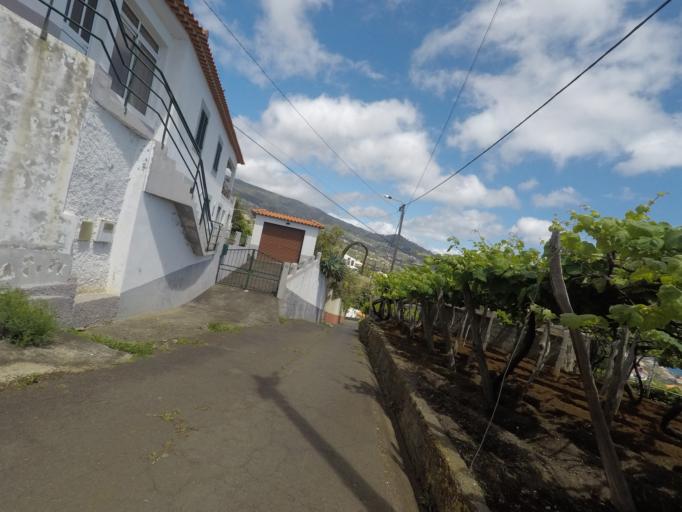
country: PT
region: Madeira
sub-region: Calheta
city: Estreito da Calheta
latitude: 32.7371
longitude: -17.1910
